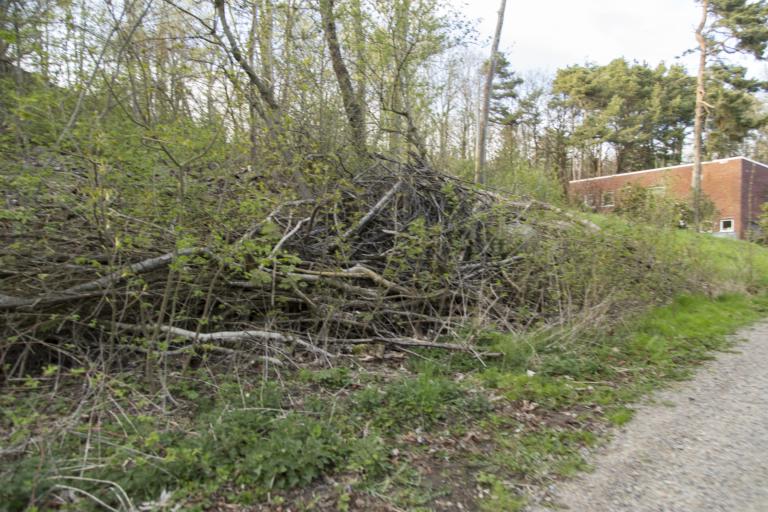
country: SE
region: Halland
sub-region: Varbergs Kommun
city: Traslovslage
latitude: 57.1050
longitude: 12.3087
